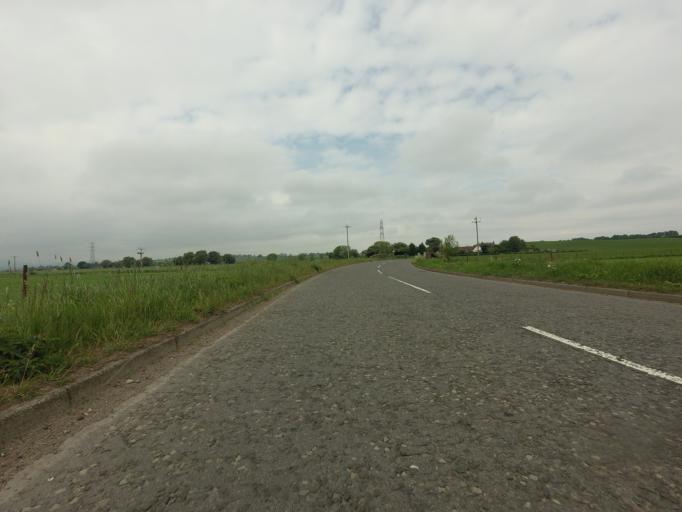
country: GB
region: Scotland
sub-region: Perth and Kinross
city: Kinross
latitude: 56.1666
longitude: -3.4476
